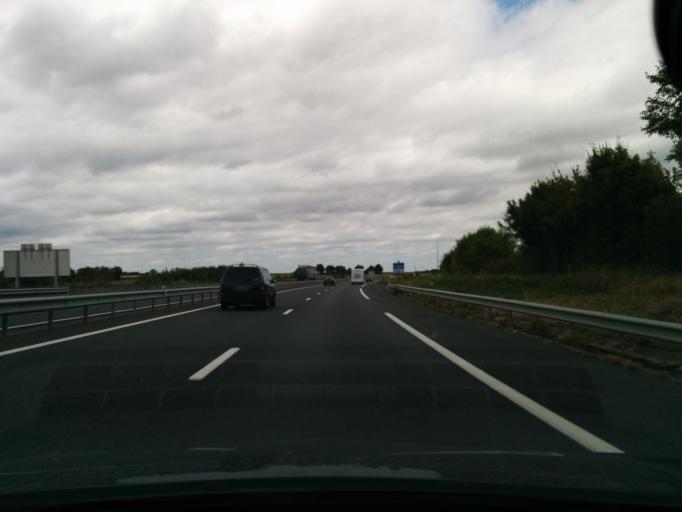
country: FR
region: Centre
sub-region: Departement de l'Indre
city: Argenton-sur-Creuse
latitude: 46.5394
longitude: 1.5084
